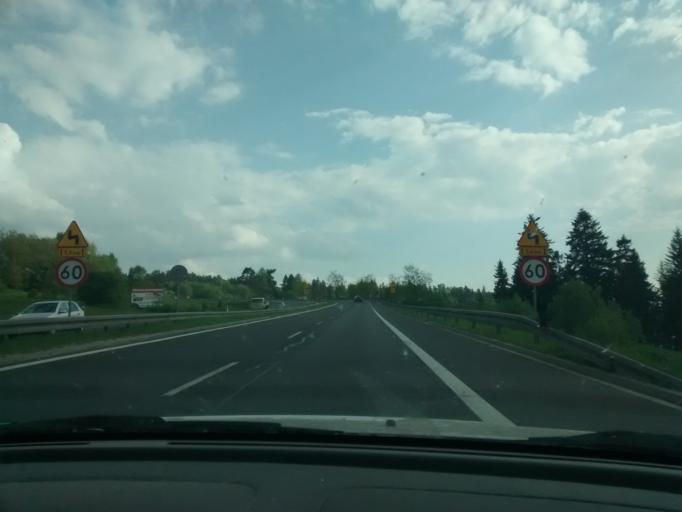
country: PL
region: Lesser Poland Voivodeship
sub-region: Powiat nowotarski
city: Rokiciny
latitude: 49.5881
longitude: 19.9324
